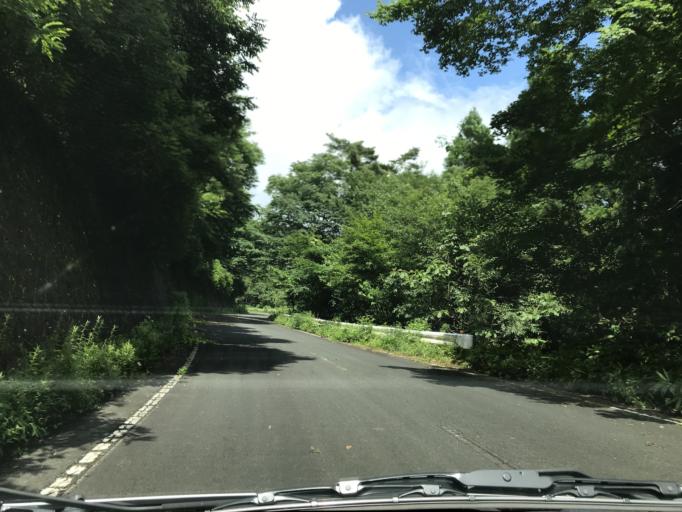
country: JP
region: Iwate
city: Tono
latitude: 39.0944
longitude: 141.4163
